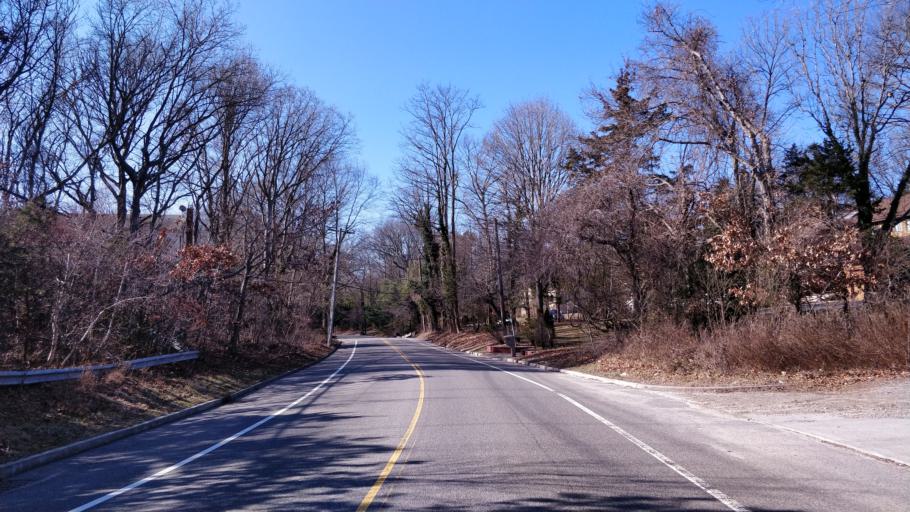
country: US
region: New York
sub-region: Suffolk County
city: Setauket-East Setauket
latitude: 40.9219
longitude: -73.0876
